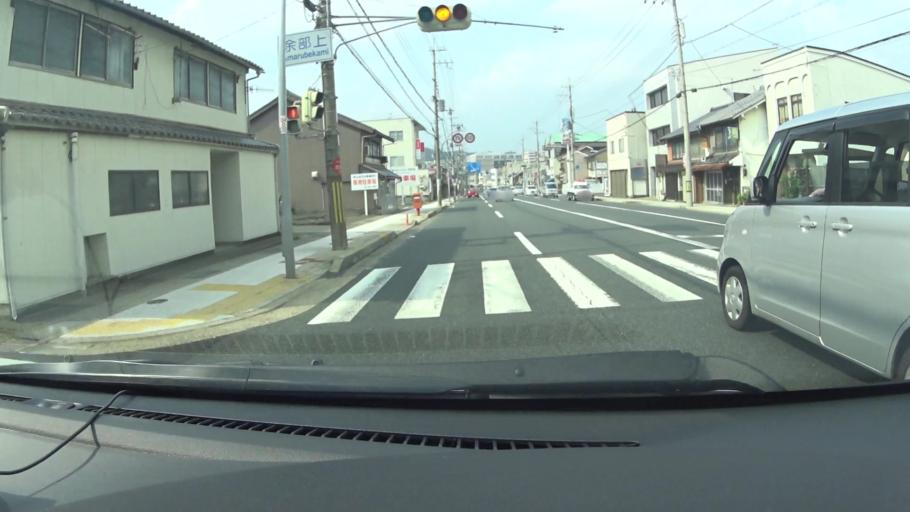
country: JP
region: Kyoto
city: Maizuru
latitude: 35.4717
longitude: 135.3660
